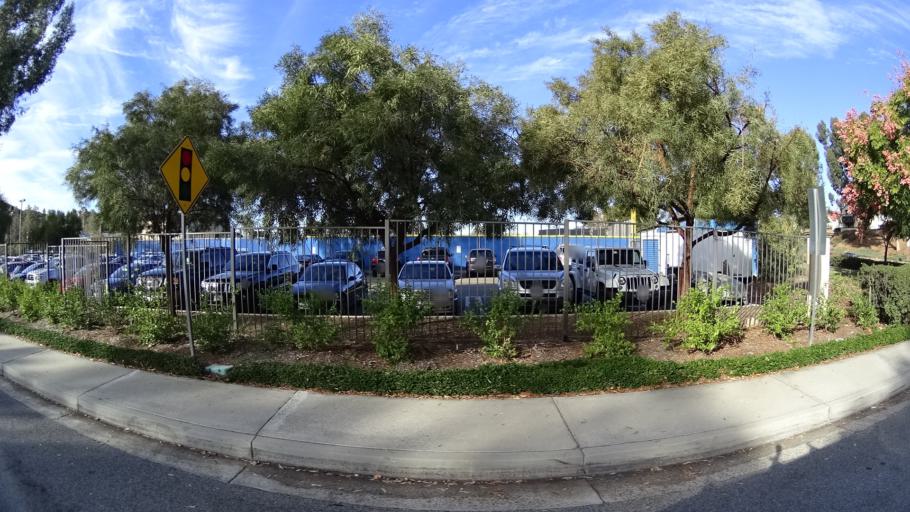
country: US
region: California
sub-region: Orange County
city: Trabuco Canyon
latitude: 33.6442
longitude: -117.5780
